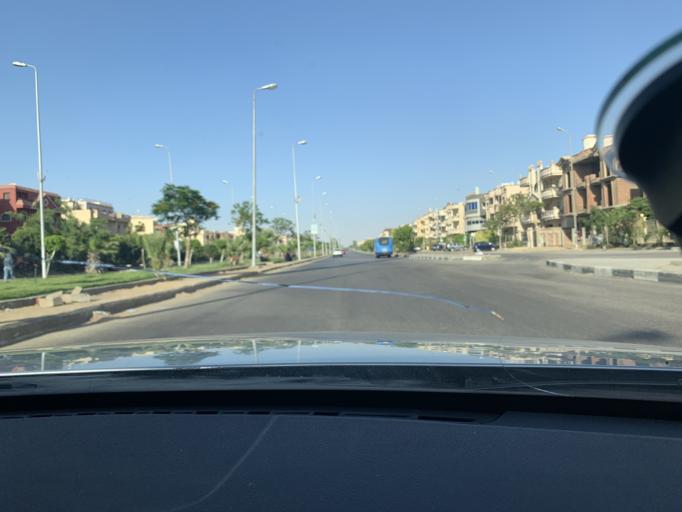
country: EG
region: Muhafazat al Qalyubiyah
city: Al Khankah
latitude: 30.0519
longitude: 31.4446
